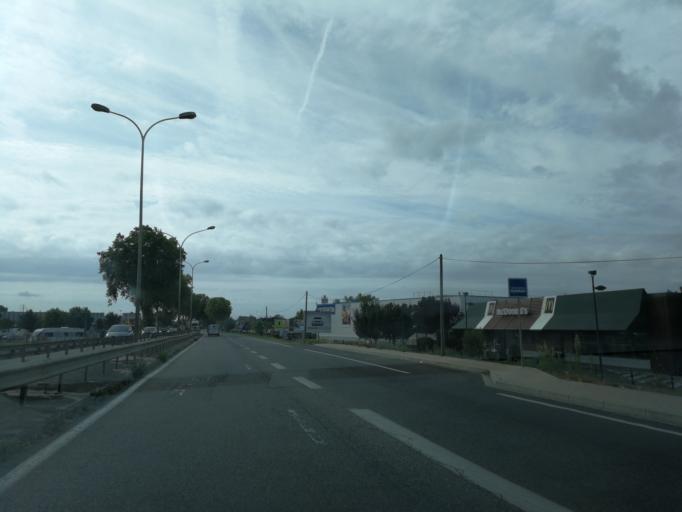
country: FR
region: Midi-Pyrenees
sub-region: Departement de la Haute-Garonne
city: Saint-Alban
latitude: 43.6873
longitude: 1.4052
